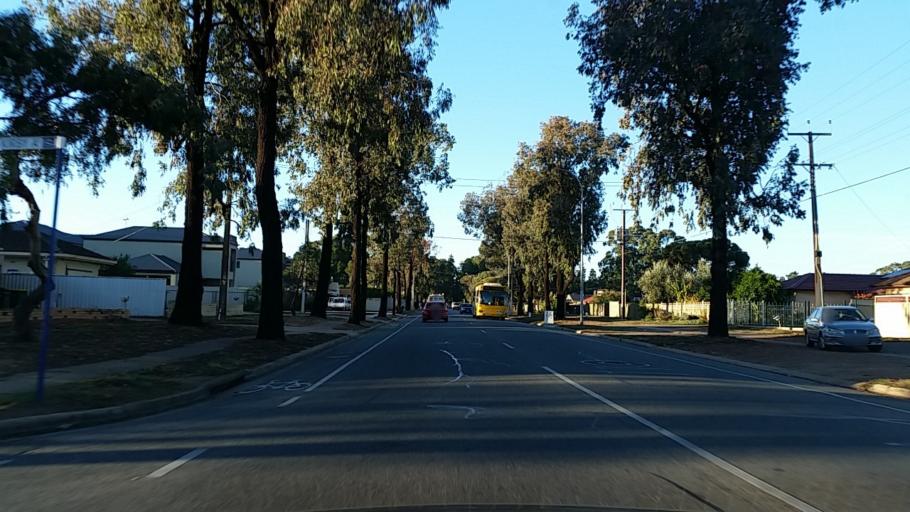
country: AU
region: South Australia
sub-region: Salisbury
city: Salisbury
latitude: -34.7621
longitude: 138.6575
